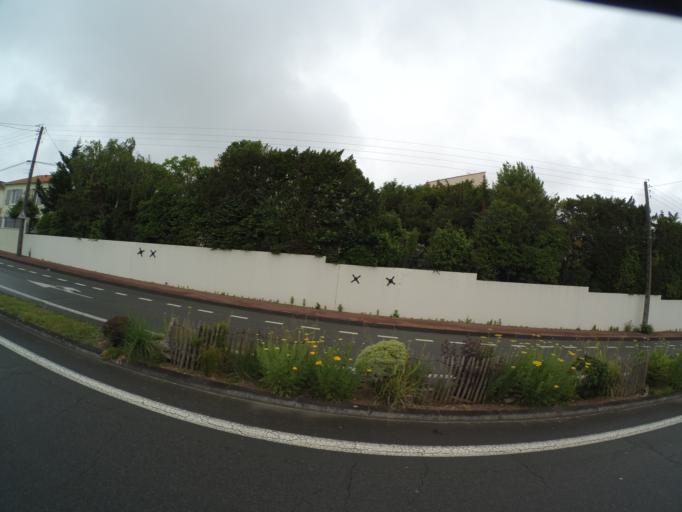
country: FR
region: Poitou-Charentes
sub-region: Departement de la Charente-Maritime
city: Saint-Georges-de-Didonne
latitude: 45.6202
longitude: -1.0078
